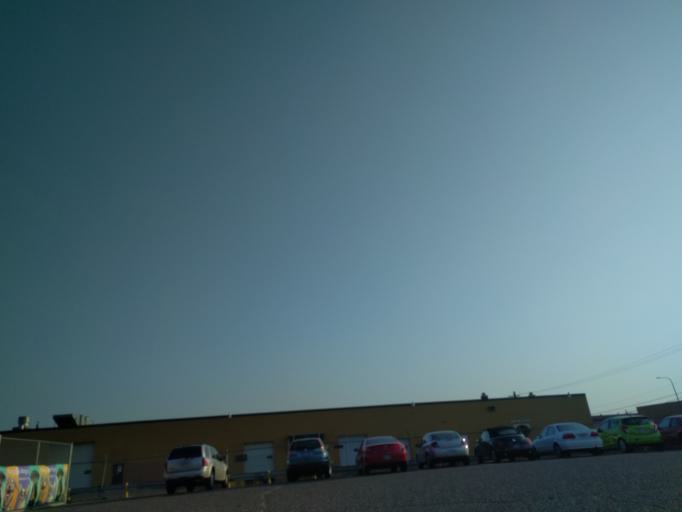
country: US
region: Minnesota
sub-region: Ramsey County
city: Falcon Heights
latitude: 44.9676
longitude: -93.1883
